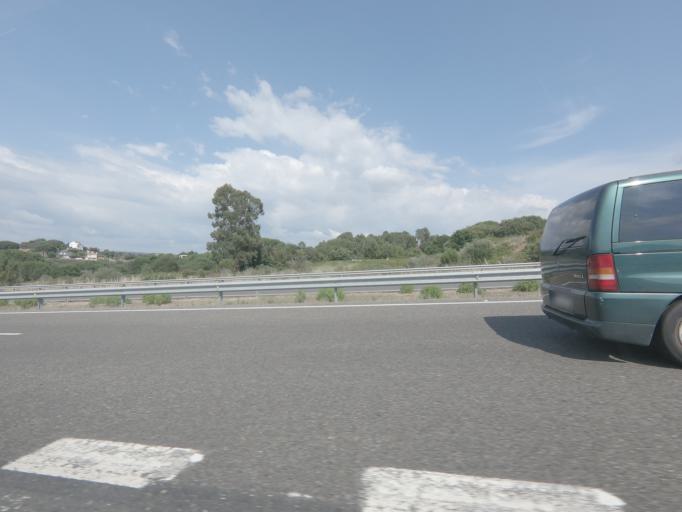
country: ES
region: Galicia
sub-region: Provincia de Ourense
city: Ourense
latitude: 42.3019
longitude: -7.8756
